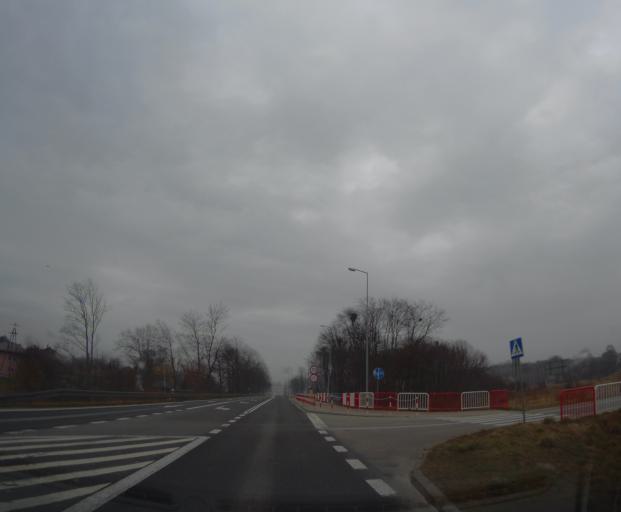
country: PL
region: Lublin Voivodeship
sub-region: Powiat bilgorajski
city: Goraj
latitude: 50.7204
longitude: 22.6729
